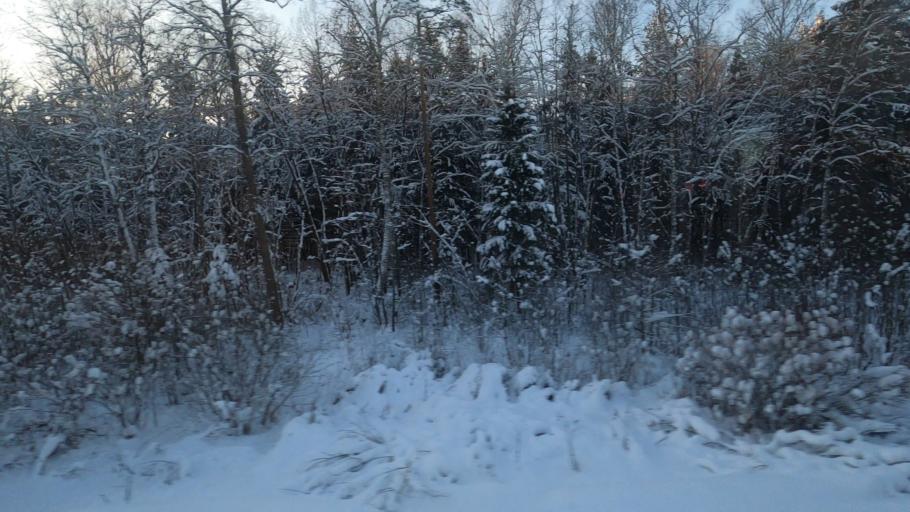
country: RU
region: Moskovskaya
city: Novo-Nikol'skoye
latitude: 56.6075
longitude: 37.5681
